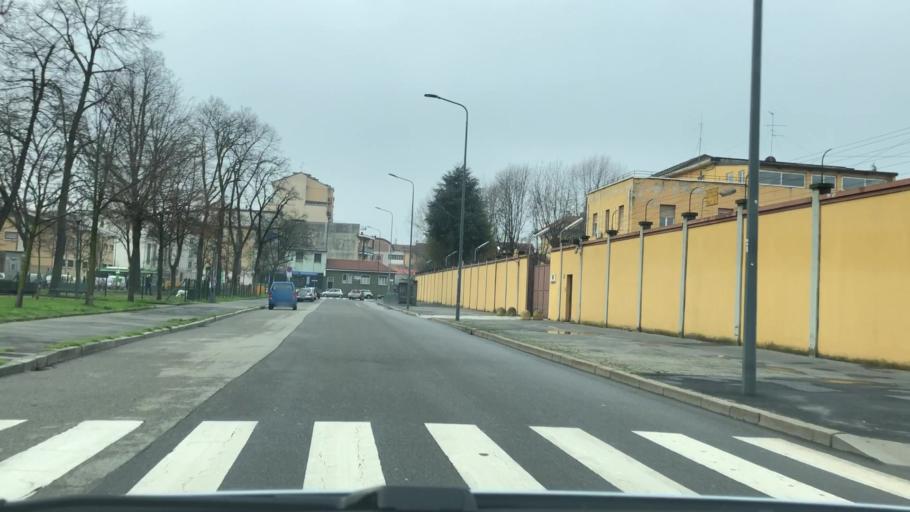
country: IT
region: Lombardy
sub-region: Citta metropolitana di Milano
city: Novegro-Tregarezzo-San Felice
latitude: 45.4753
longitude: 9.2474
